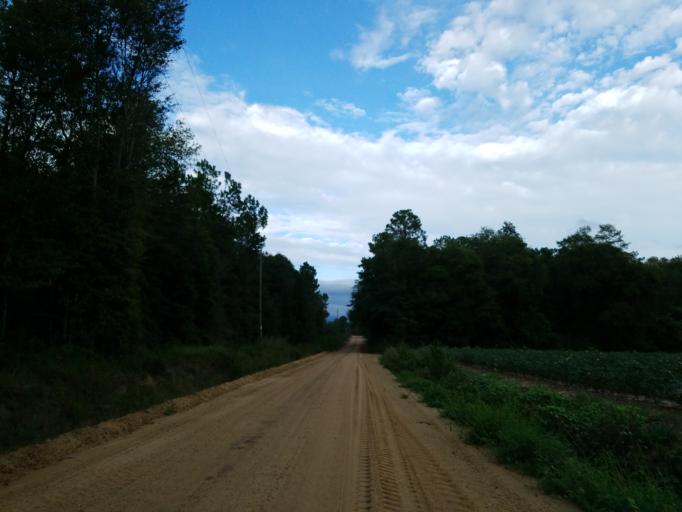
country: US
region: Georgia
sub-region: Cook County
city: Sparks
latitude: 31.2354
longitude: -83.4498
